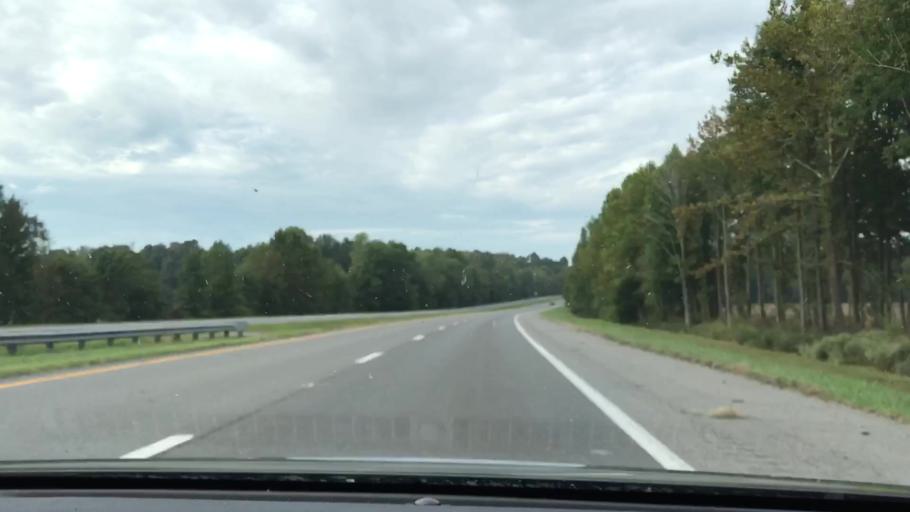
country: US
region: Kentucky
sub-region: Marshall County
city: Benton
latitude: 36.8048
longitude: -88.4952
